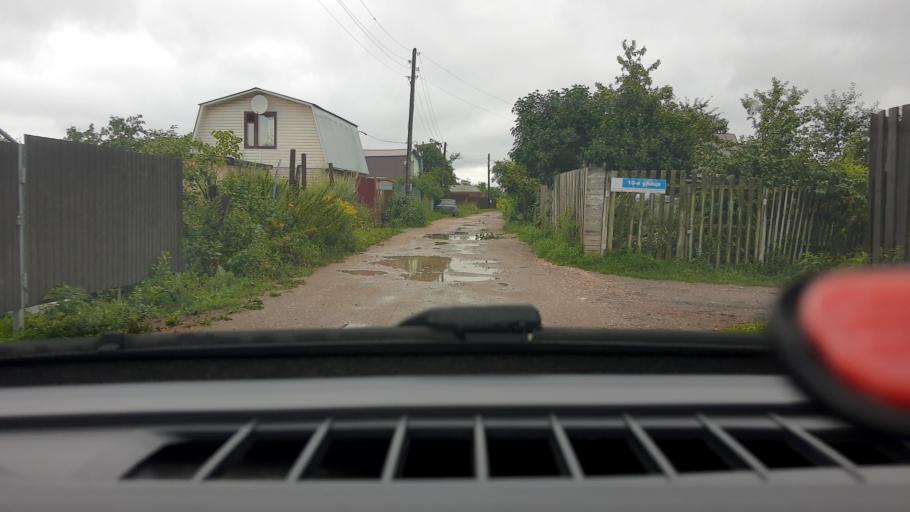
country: RU
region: Nizjnij Novgorod
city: Gorbatovka
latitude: 56.3180
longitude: 43.8364
